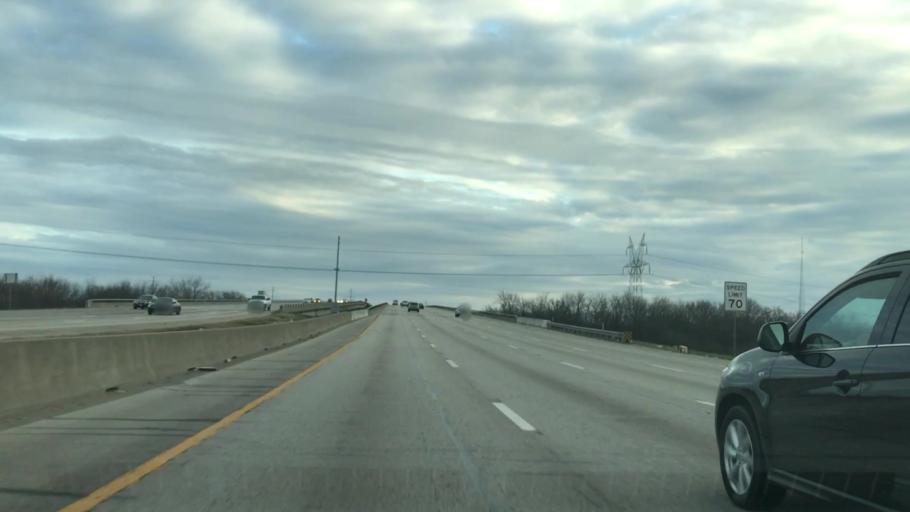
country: US
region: Texas
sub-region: Dallas County
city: Irving
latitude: 32.7903
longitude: -96.9198
